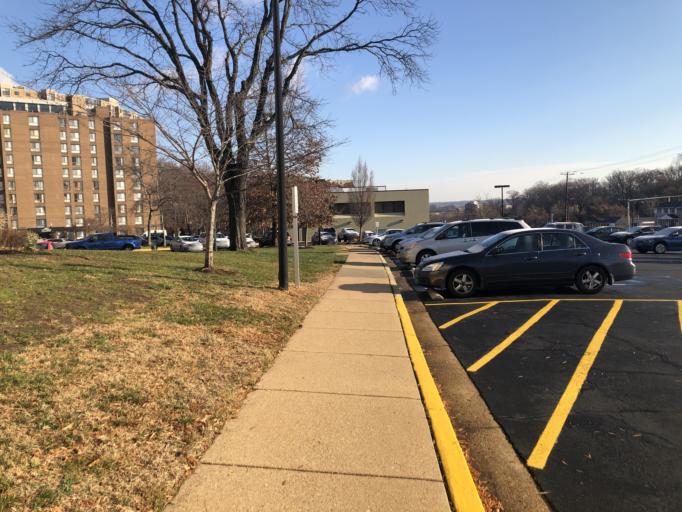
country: US
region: Virginia
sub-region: Fairfax County
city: Huntington
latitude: 38.7861
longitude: -77.0703
